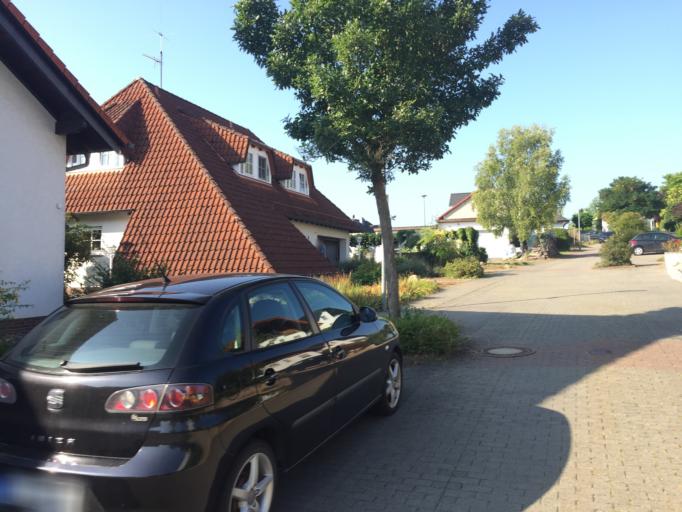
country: DE
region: Hesse
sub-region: Regierungsbezirk Giessen
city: Hoernsheim
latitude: 50.4644
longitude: 8.5871
